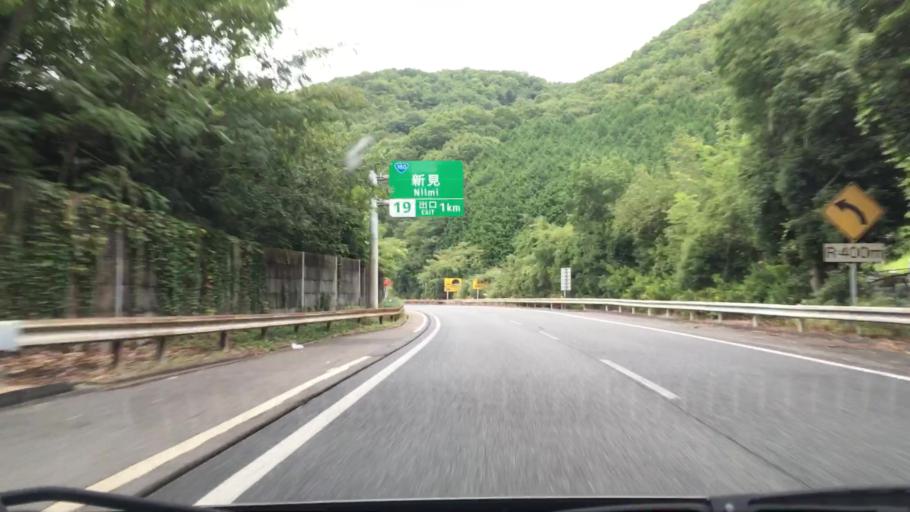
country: JP
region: Okayama
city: Niimi
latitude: 34.9917
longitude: 133.4593
